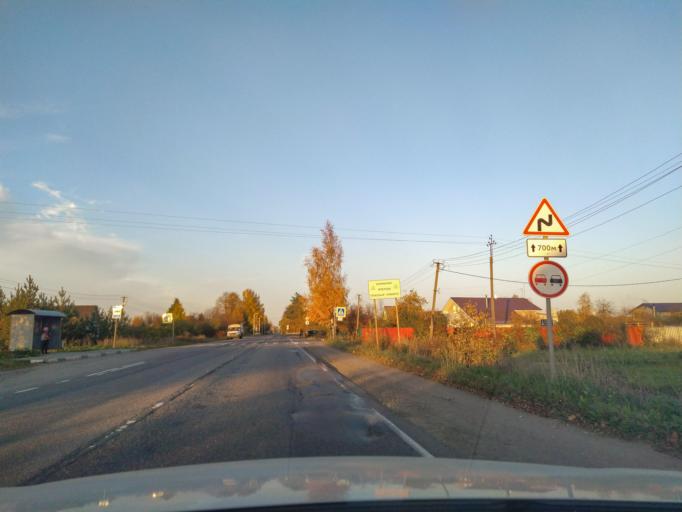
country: RU
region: Leningrad
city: Maloye Verevo
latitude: 59.6164
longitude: 30.2076
